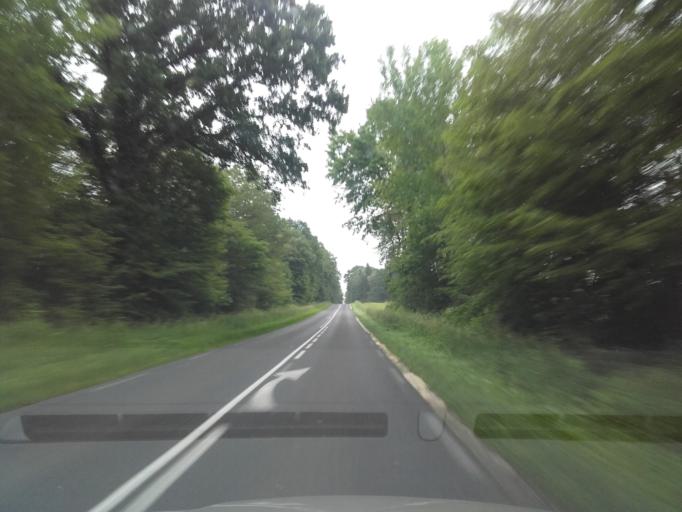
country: FR
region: Centre
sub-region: Departement d'Indre-et-Loire
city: Beaumont-la-Ronce
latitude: 47.5923
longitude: 0.6647
